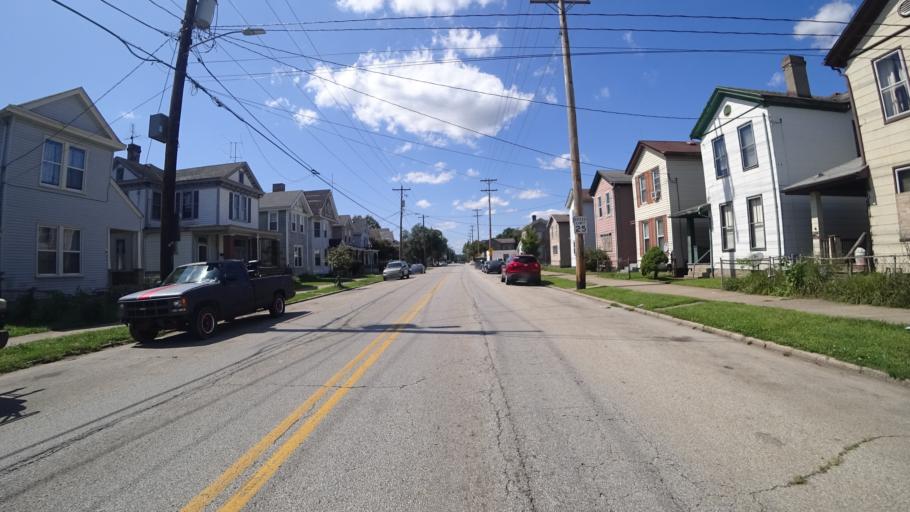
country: US
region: Ohio
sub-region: Butler County
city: Hamilton
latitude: 39.4016
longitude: -84.5497
